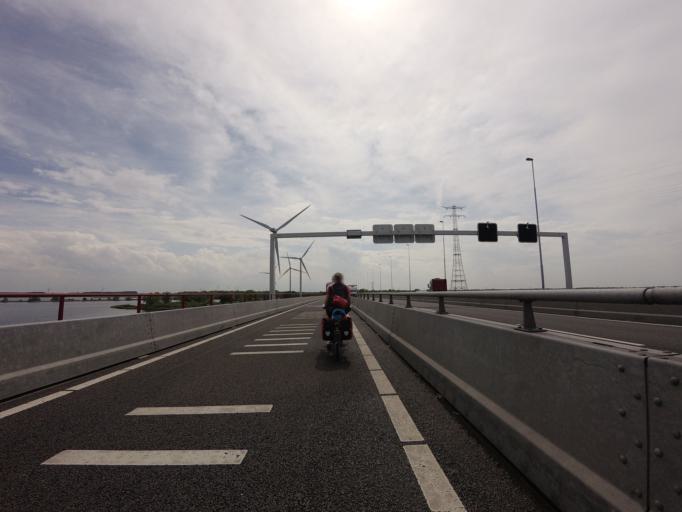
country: NL
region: North Brabant
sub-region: Gemeente Moerdijk
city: Willemstad
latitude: 51.7133
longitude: 4.3994
